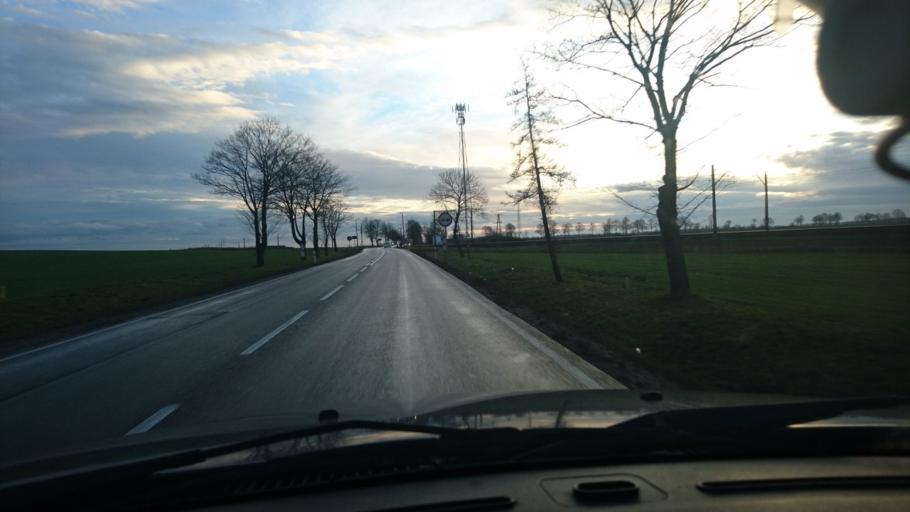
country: PL
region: Opole Voivodeship
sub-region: Powiat kluczborski
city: Byczyna
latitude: 51.0997
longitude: 18.2046
